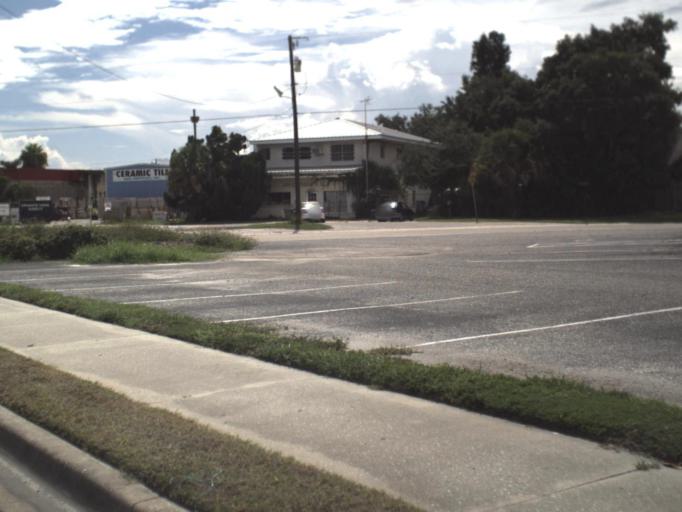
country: US
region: Florida
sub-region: Sarasota County
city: Venice
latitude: 27.0952
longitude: -82.4337
